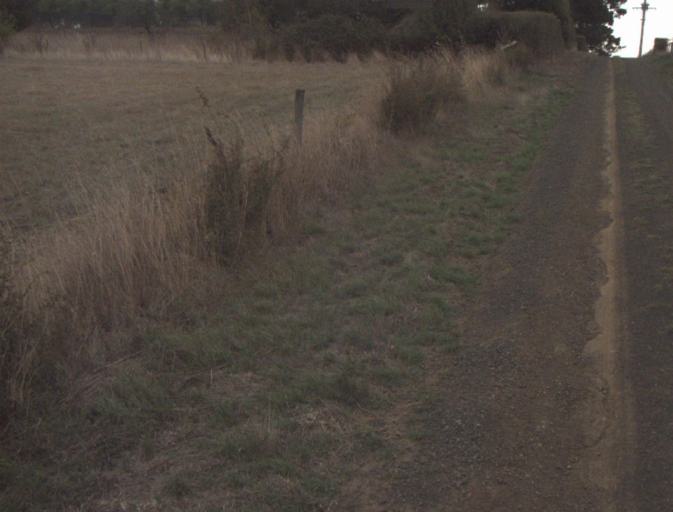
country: AU
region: Tasmania
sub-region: Northern Midlands
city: Evandale
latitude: -41.5145
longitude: 147.2568
